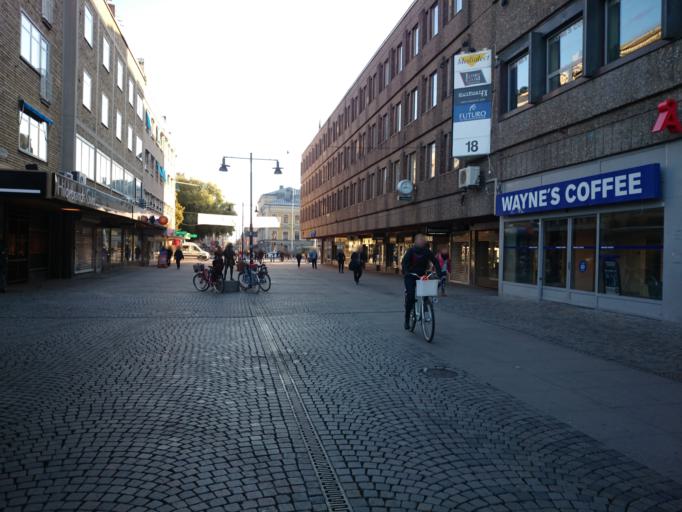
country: SE
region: Gaevleborg
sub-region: Gavle Kommun
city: Gavle
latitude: 60.6743
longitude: 17.1426
